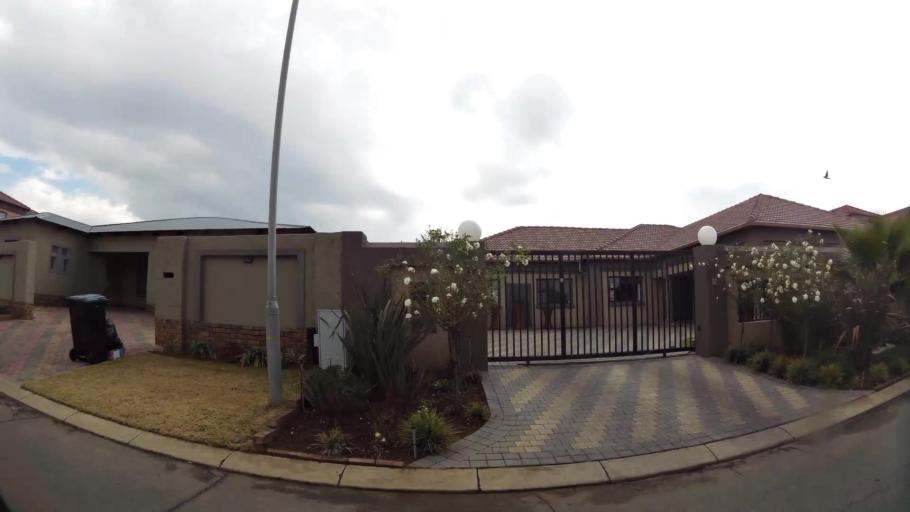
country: ZA
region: Gauteng
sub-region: Sedibeng District Municipality
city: Vanderbijlpark
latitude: -26.7282
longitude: 27.8691
